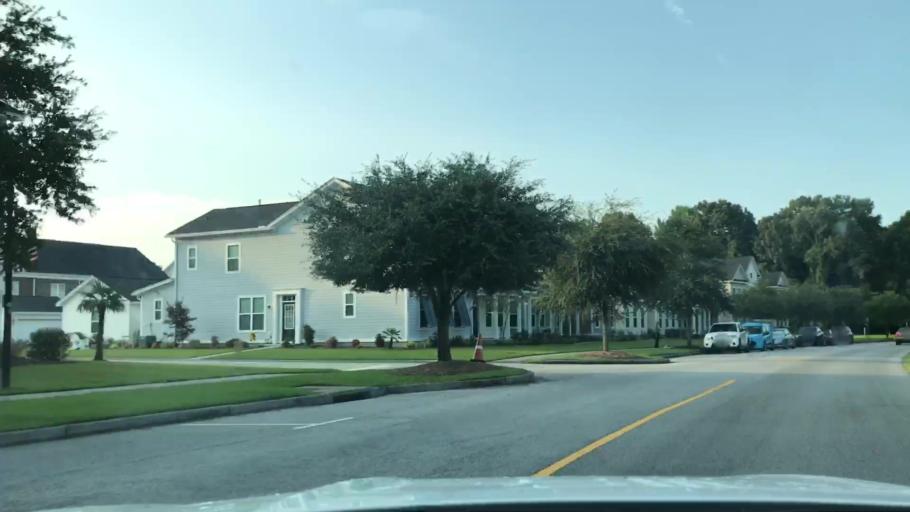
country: US
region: South Carolina
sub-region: Charleston County
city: Shell Point
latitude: 32.8347
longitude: -80.0905
